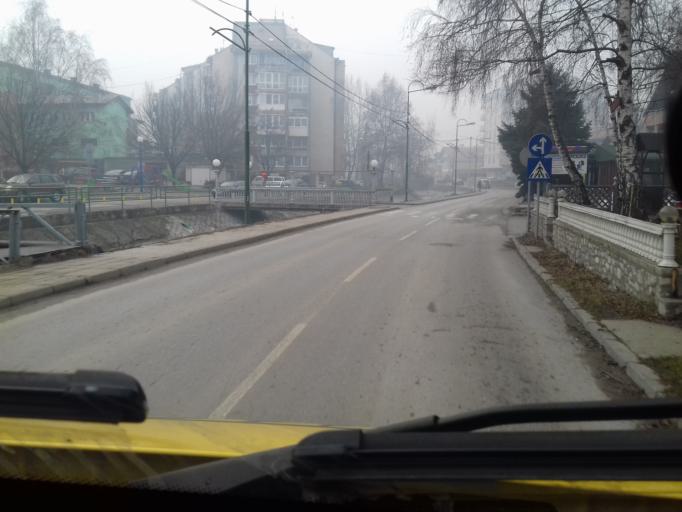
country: BA
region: Federation of Bosnia and Herzegovina
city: Kakanj
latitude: 44.1255
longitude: 18.1148
